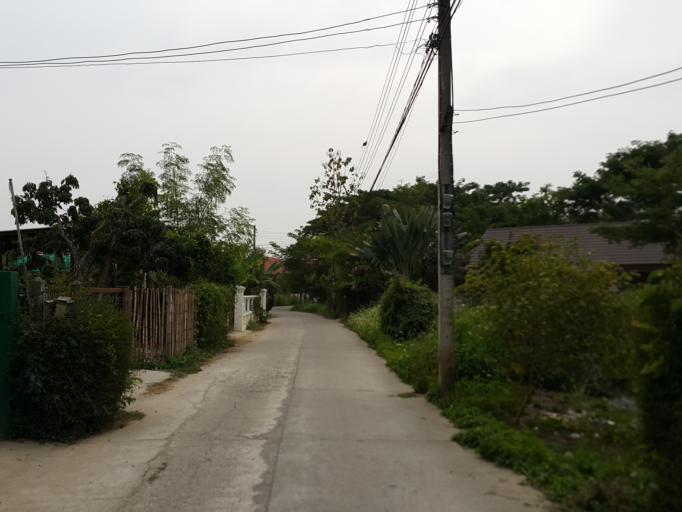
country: TH
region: Chiang Mai
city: Saraphi
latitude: 18.7378
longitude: 99.0223
